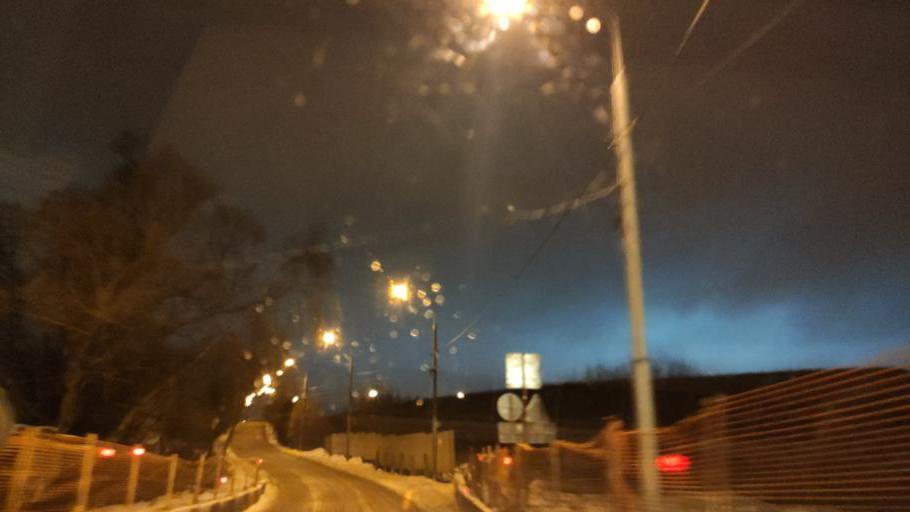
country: RU
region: Moskovskaya
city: Annino
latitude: 55.5813
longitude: 37.2626
